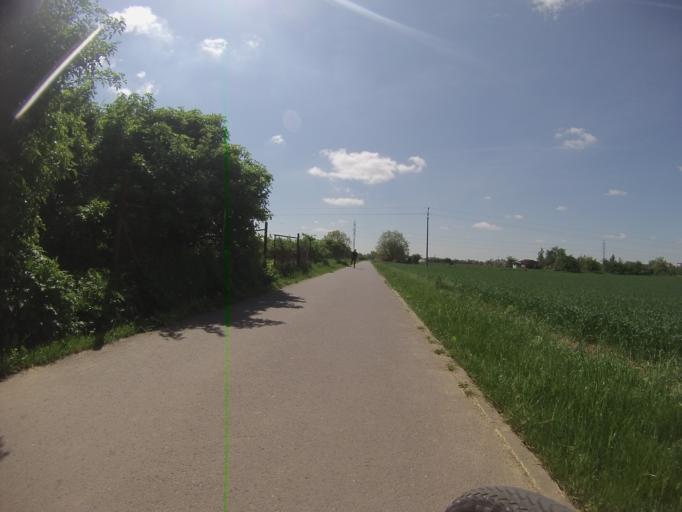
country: CZ
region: South Moravian
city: Modrice
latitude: 49.1365
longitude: 16.6248
